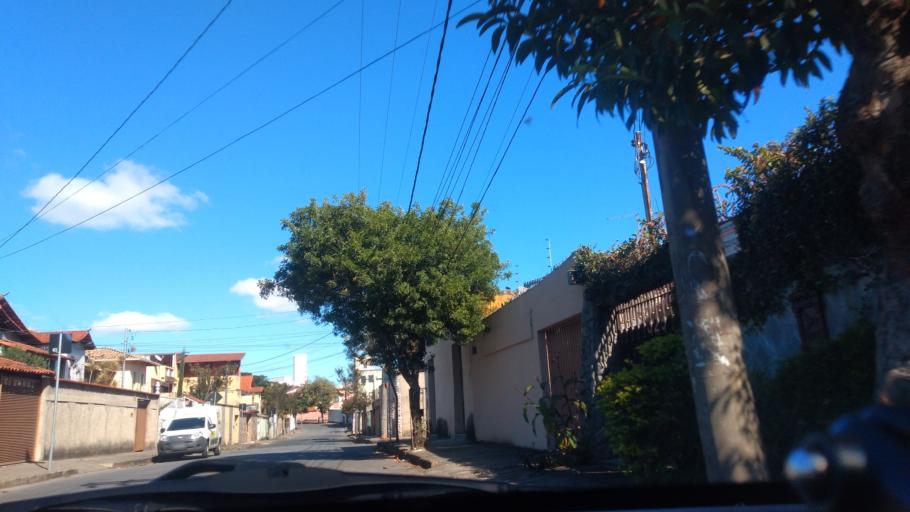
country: BR
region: Minas Gerais
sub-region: Belo Horizonte
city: Belo Horizonte
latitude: -19.8393
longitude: -43.9474
